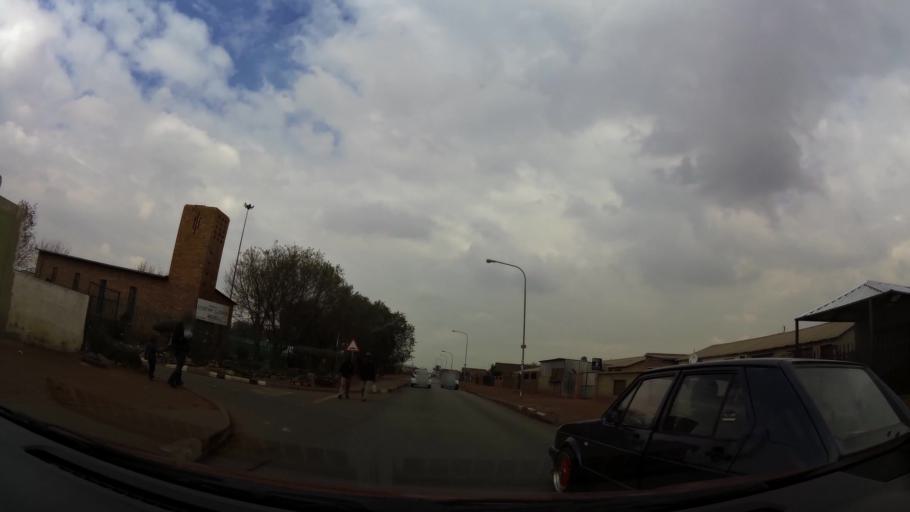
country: ZA
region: Gauteng
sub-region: City of Johannesburg Metropolitan Municipality
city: Soweto
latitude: -26.2552
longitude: 27.8328
